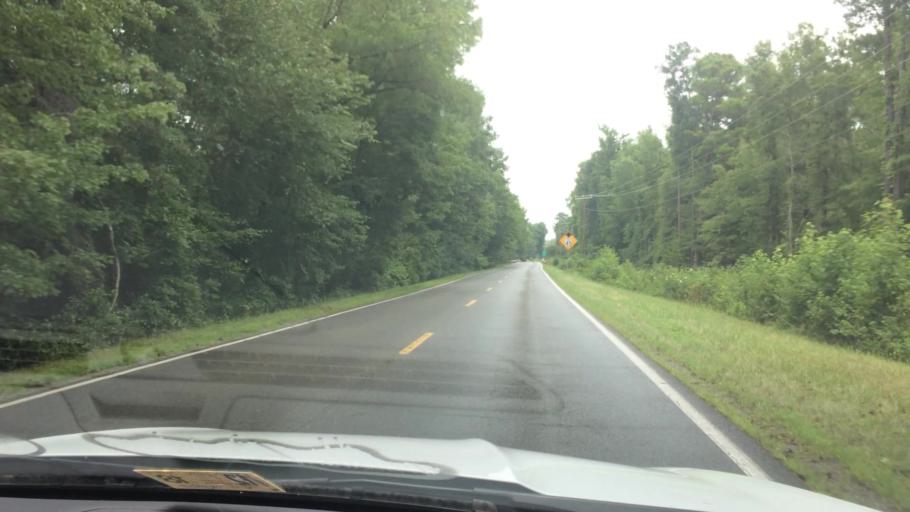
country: US
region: Virginia
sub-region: Charles City County
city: Charles City
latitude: 37.4266
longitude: -77.0391
